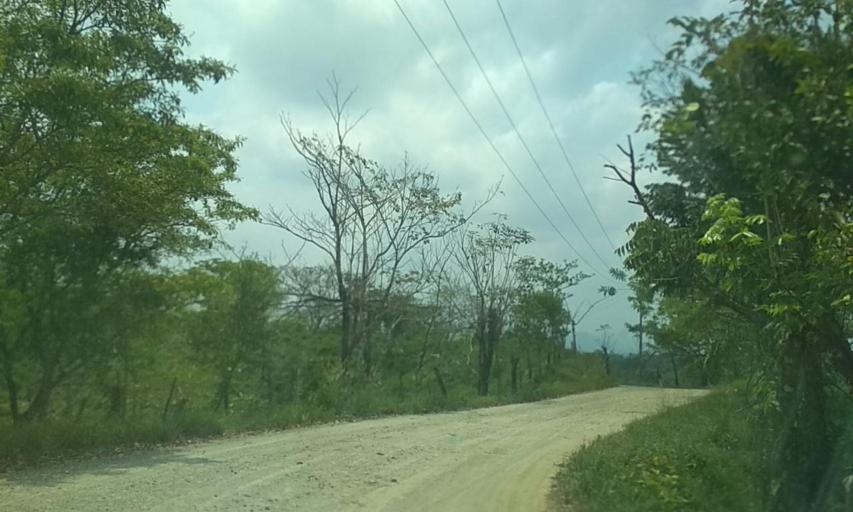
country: MX
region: Tabasco
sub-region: Huimanguillo
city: Francisco Rueda
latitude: 17.6116
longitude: -93.8109
